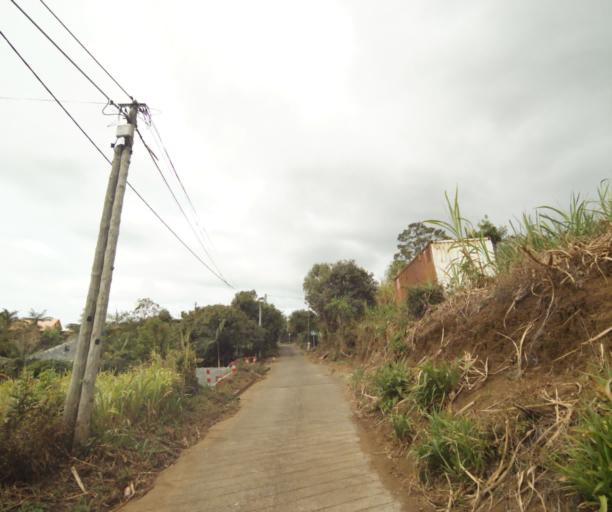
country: RE
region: Reunion
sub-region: Reunion
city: Saint-Paul
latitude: -21.0173
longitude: 55.3289
